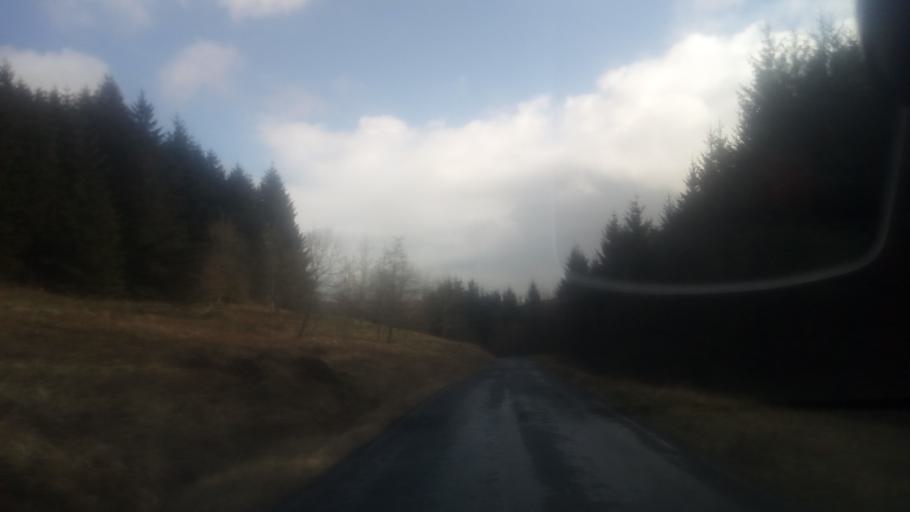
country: GB
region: Scotland
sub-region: The Scottish Borders
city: Innerleithen
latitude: 55.4677
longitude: -3.1380
